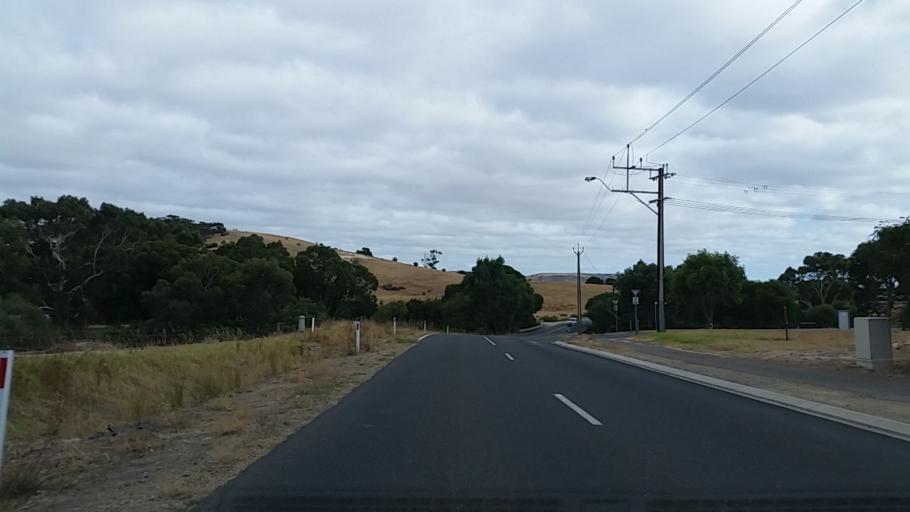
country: AU
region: South Australia
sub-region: Yankalilla
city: Normanville
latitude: -35.4308
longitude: 138.3254
